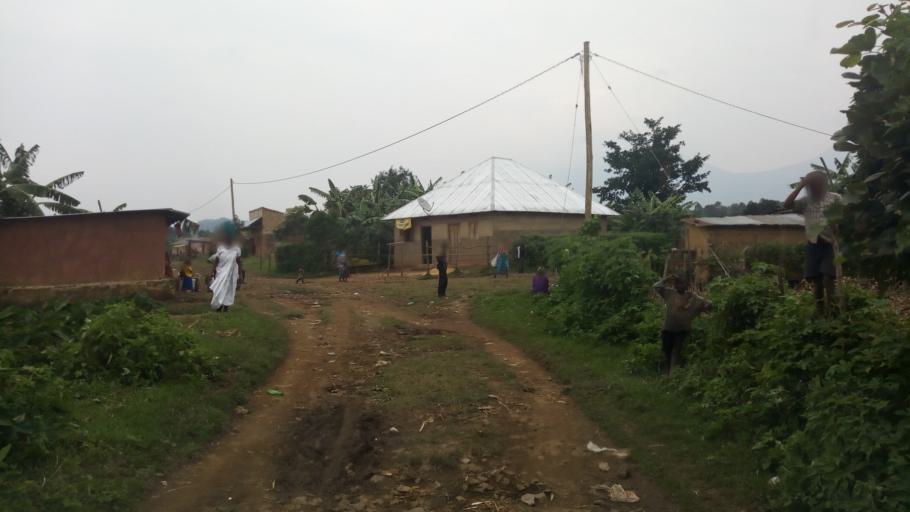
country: UG
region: Western Region
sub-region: Kisoro District
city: Kisoro
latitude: -1.2714
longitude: 29.6163
